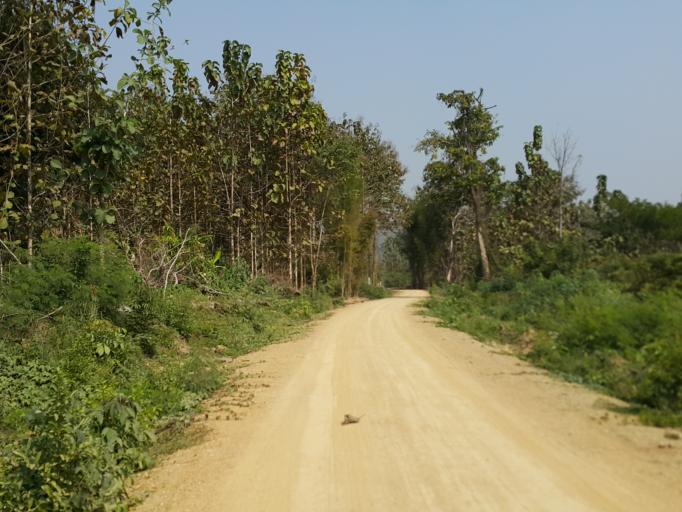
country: TH
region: Sukhothai
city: Thung Saliam
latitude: 17.3348
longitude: 99.4599
